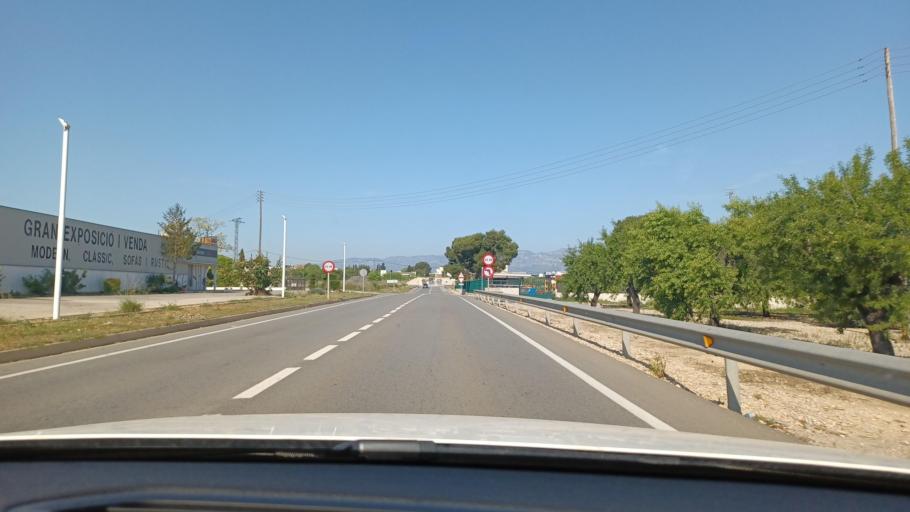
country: ES
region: Catalonia
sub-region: Provincia de Tarragona
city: Santa Barbara
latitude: 40.7170
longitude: 0.5092
